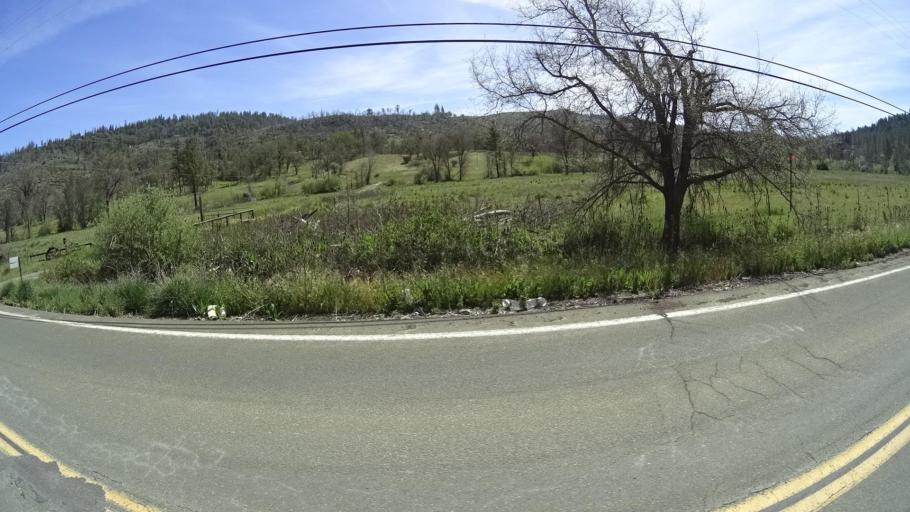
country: US
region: California
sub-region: Lake County
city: Cobb
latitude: 38.8393
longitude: -122.7469
